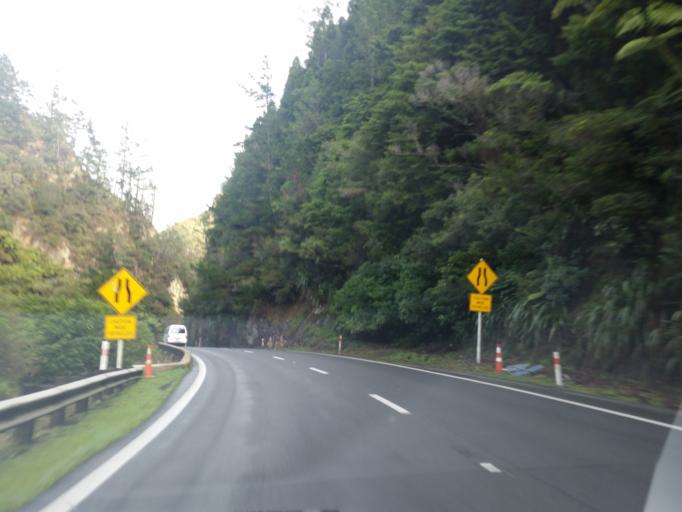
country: NZ
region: Waikato
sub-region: Hauraki District
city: Paeroa
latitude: -37.4203
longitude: 175.7344
